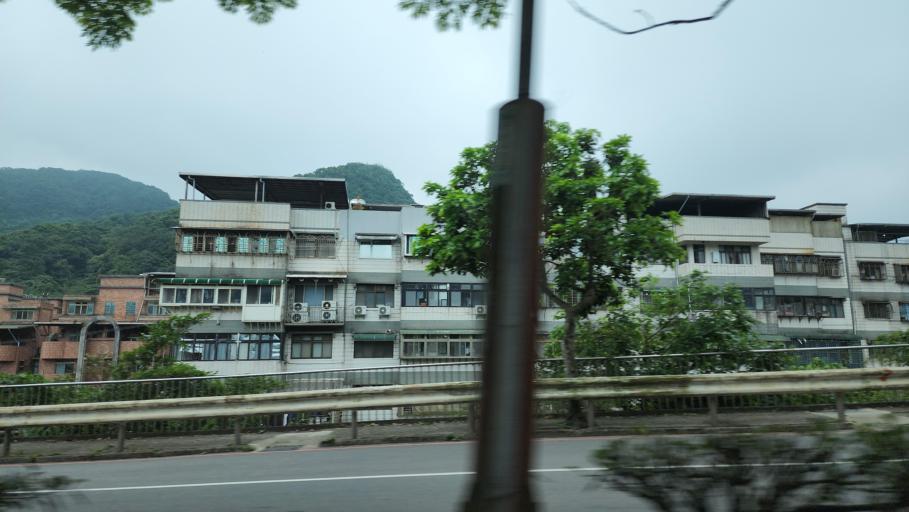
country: TW
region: Taiwan
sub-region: Keelung
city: Keelung
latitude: 25.1586
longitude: 121.6944
